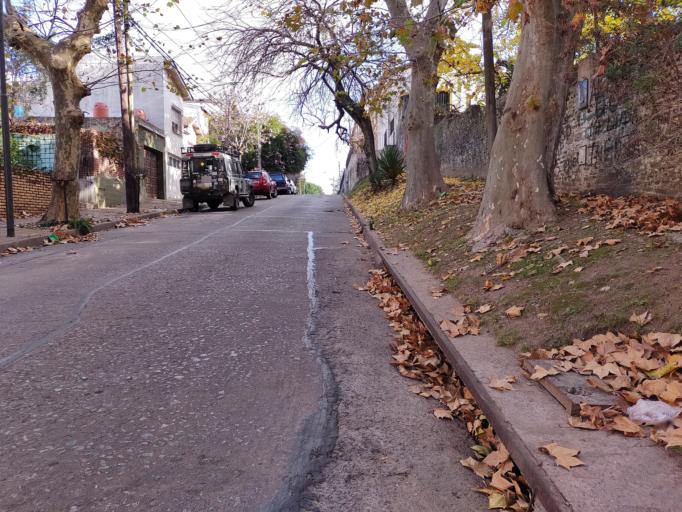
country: AR
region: Buenos Aires
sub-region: Partido de Tigre
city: Tigre
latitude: -34.4428
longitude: -58.5480
